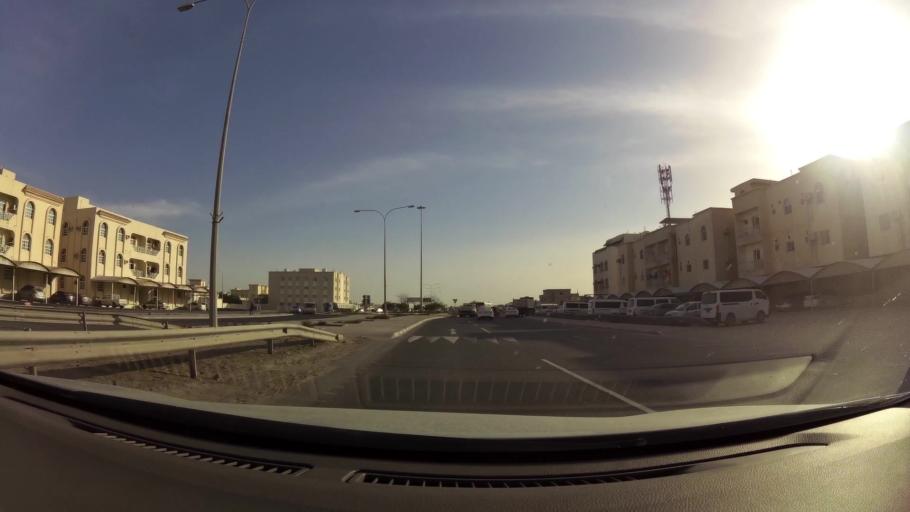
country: QA
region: Al Wakrah
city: Al Wakrah
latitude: 25.1516
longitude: 51.6028
